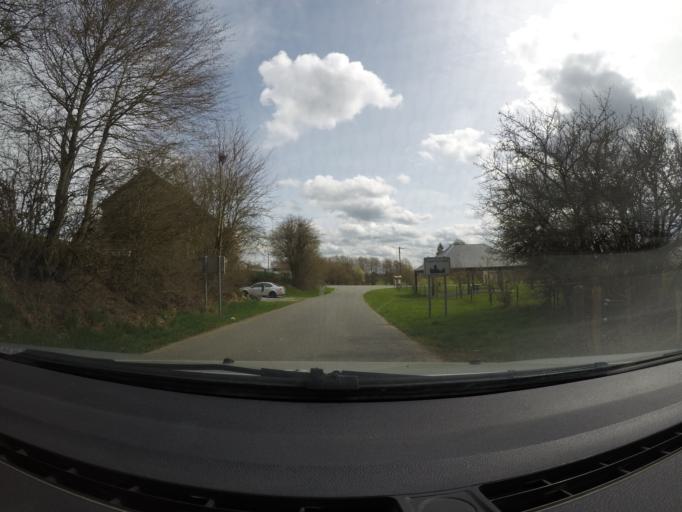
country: BE
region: Wallonia
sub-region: Province du Luxembourg
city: Neufchateau
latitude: 49.8182
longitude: 5.4706
